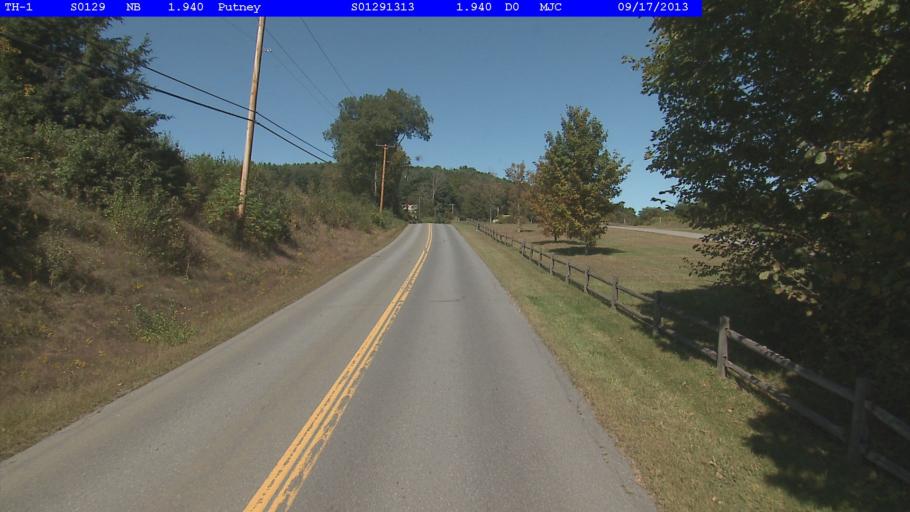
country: US
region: New Hampshire
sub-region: Cheshire County
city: Westmoreland
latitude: 43.0005
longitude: -72.5326
